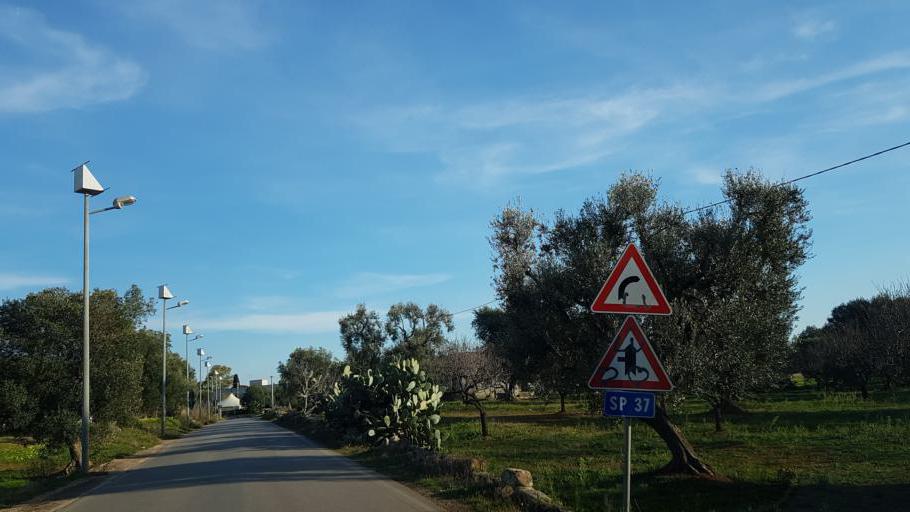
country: IT
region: Apulia
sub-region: Provincia di Brindisi
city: San Vito dei Normanni
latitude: 40.6941
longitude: 17.7603
